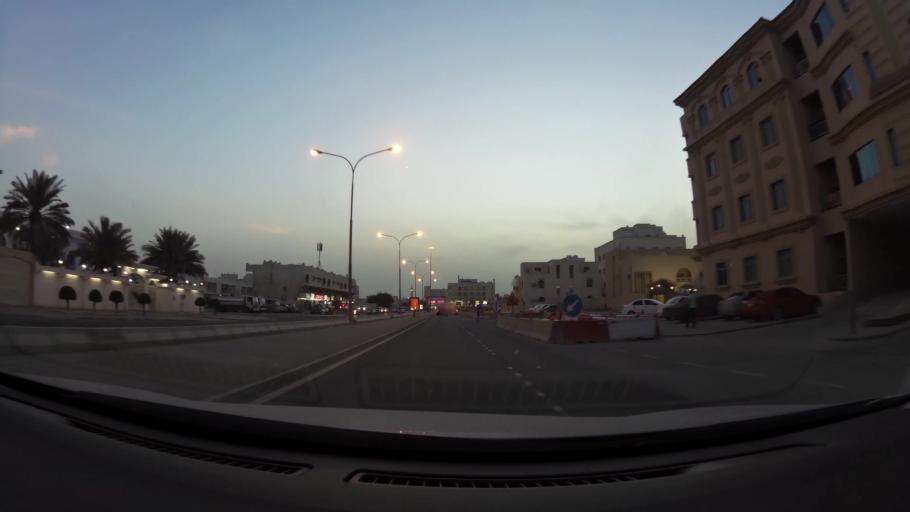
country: QA
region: Al Wakrah
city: Al Wakrah
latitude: 25.1616
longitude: 51.6008
